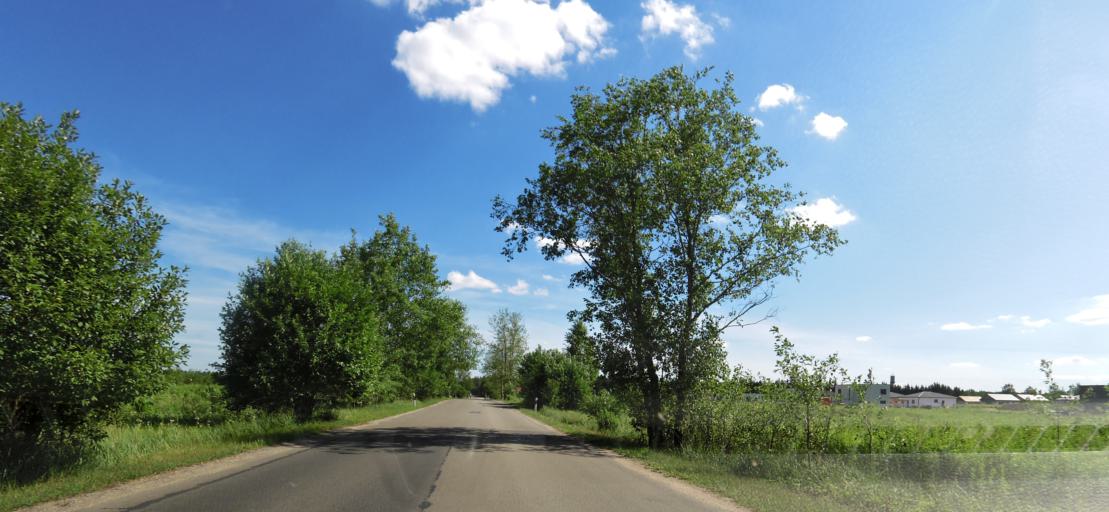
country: LT
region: Vilnius County
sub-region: Vilnius
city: Fabijoniskes
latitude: 54.8093
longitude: 25.3251
